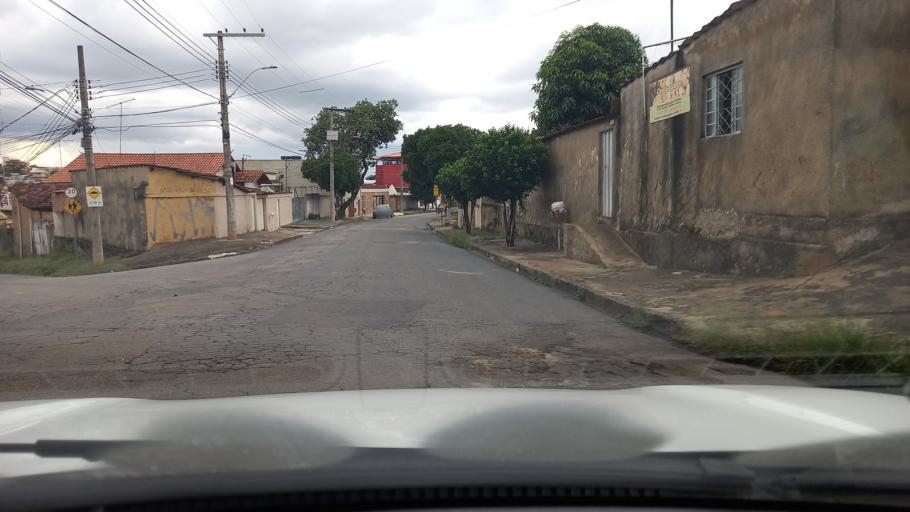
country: BR
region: Minas Gerais
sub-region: Contagem
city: Contagem
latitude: -19.8997
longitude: -44.0154
